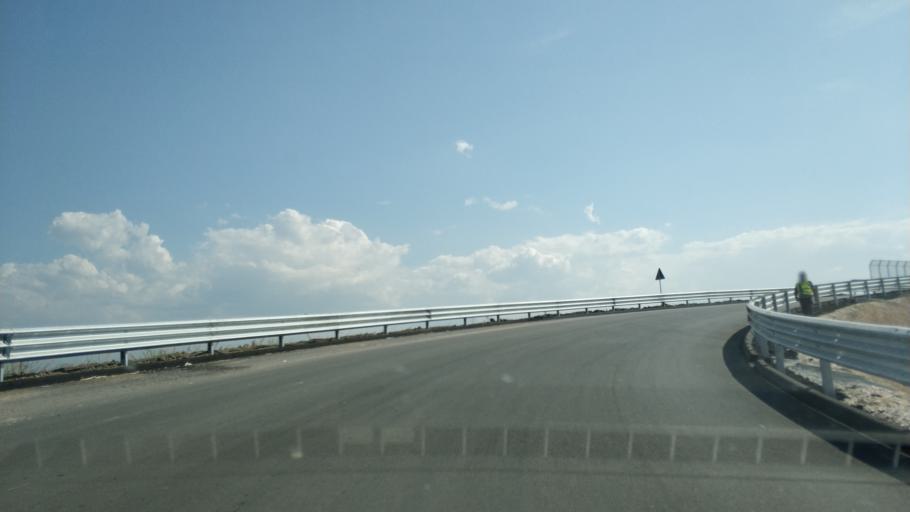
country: AL
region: Fier
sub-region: Rrethi i Fierit
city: Dermenas
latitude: 40.7415
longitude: 19.4829
